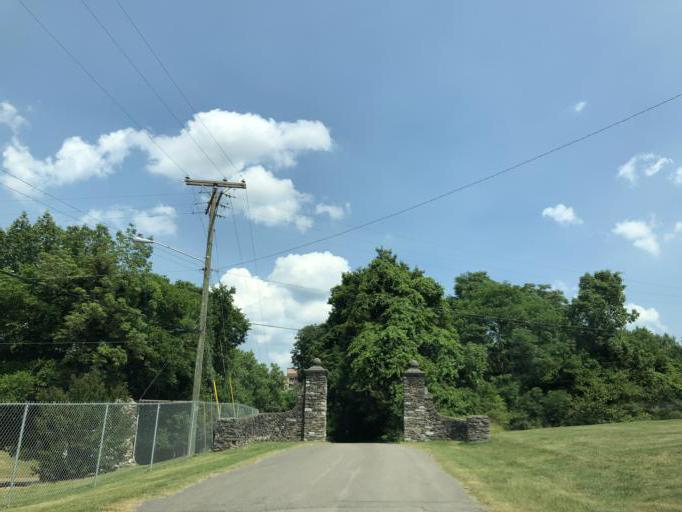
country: US
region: Tennessee
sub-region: Davidson County
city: Goodlettsville
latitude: 36.2442
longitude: -86.7212
